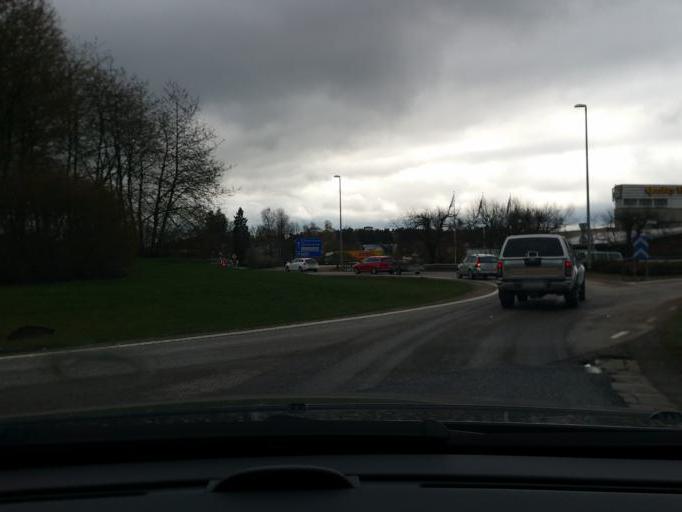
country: SE
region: Kronoberg
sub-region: Vaxjo Kommun
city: Vaexjoe
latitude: 56.8808
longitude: 14.8328
